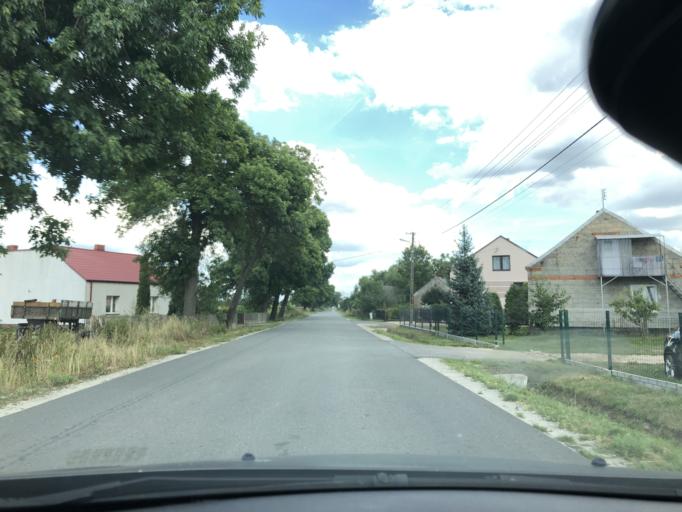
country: PL
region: Lodz Voivodeship
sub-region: Powiat wieruszowski
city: Czastary
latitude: 51.2410
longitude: 18.3487
